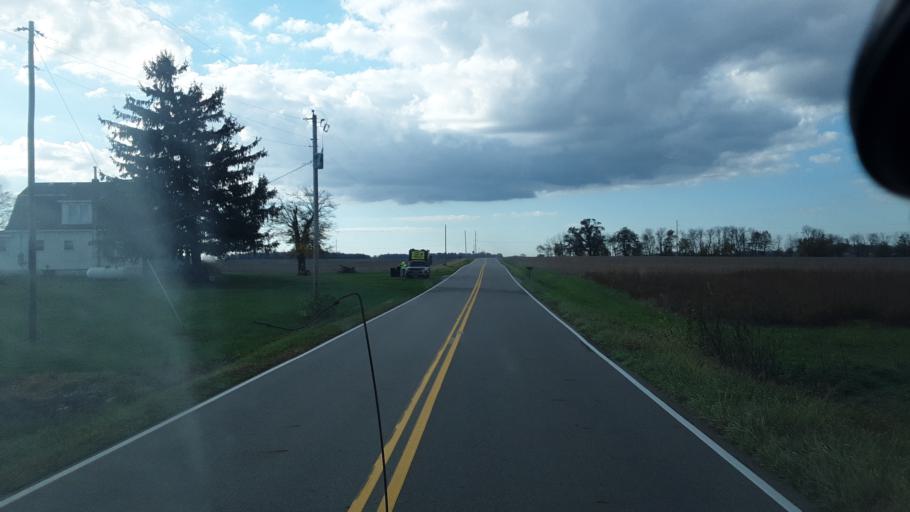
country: US
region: Ohio
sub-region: Fayette County
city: Washington Court House
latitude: 39.4387
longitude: -83.4390
